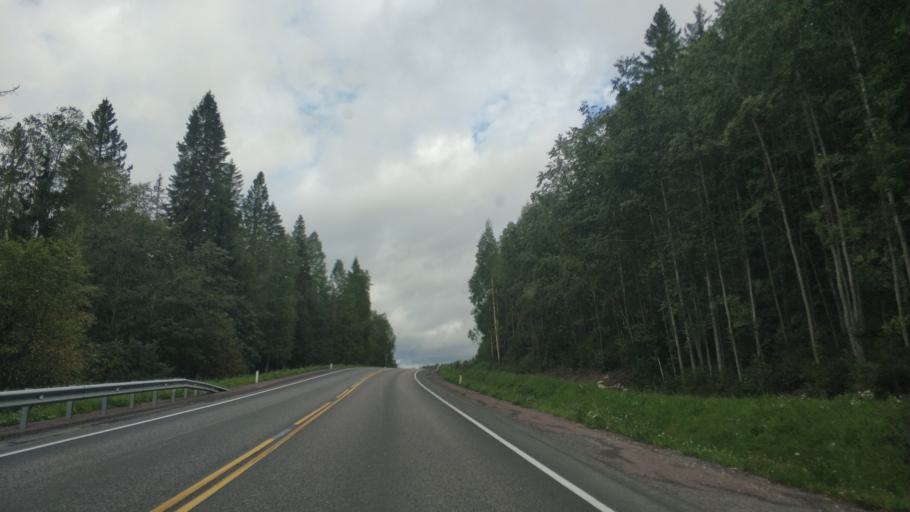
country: RU
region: Republic of Karelia
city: Khelyulya
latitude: 61.7941
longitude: 30.6246
